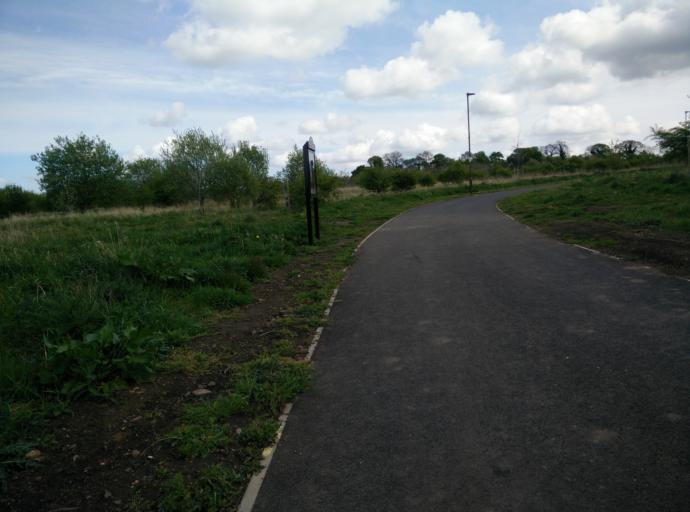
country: GB
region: Scotland
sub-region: Midlothian
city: Bonnyrigg
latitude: 55.9206
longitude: -3.1212
